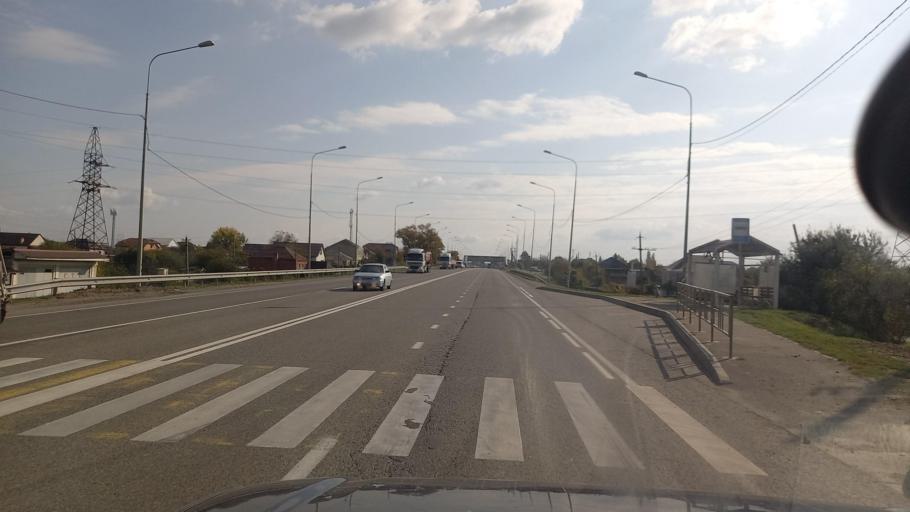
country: RU
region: Krasnodarskiy
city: Novoukrainskiy
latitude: 44.8978
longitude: 38.0439
